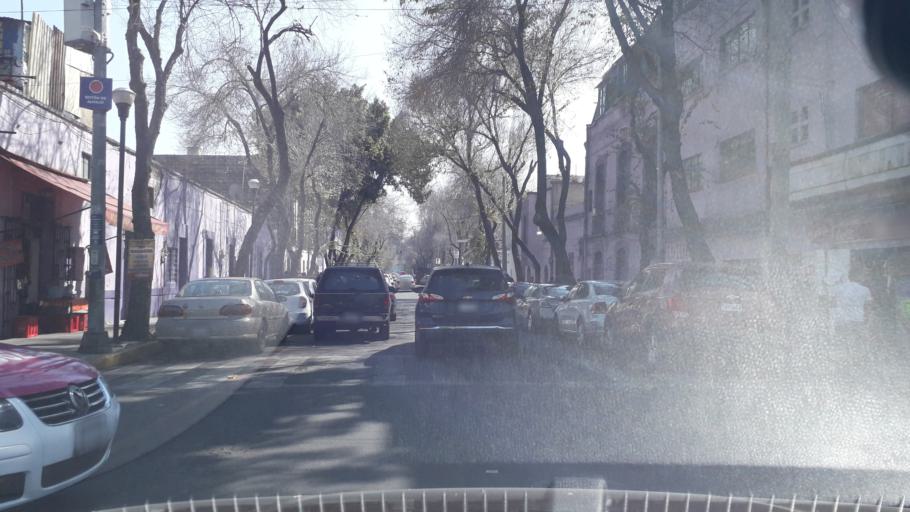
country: MX
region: Mexico City
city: Cuauhtemoc
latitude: 19.4421
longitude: -99.1512
